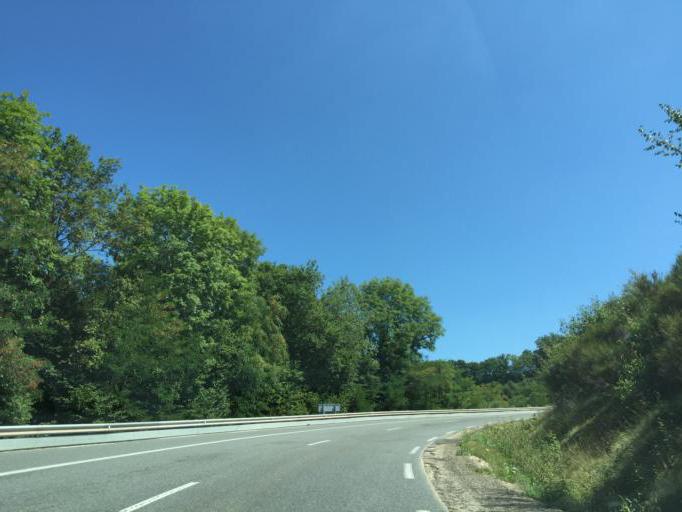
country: FR
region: Midi-Pyrenees
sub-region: Departement de l'Aveyron
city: Espalion
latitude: 44.5576
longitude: 2.7811
